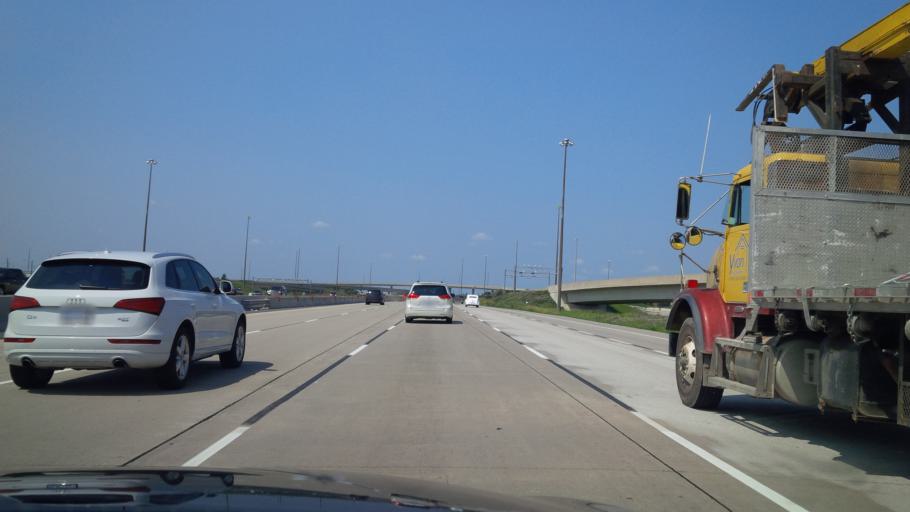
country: CA
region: Ontario
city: Etobicoke
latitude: 43.7572
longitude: -79.6215
